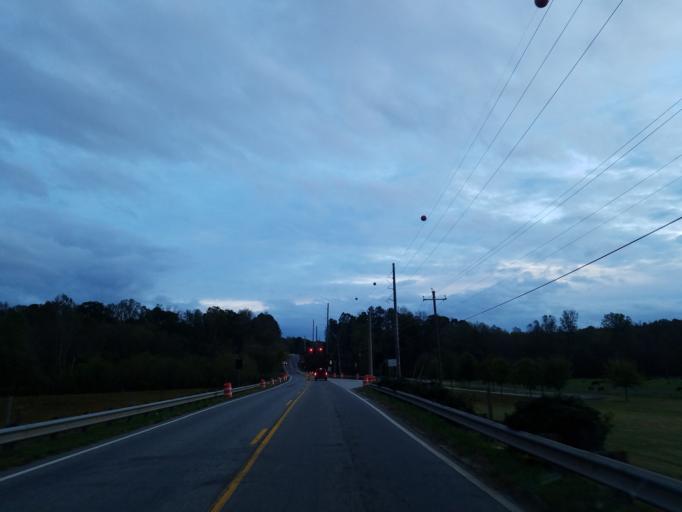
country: US
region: Georgia
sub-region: Dawson County
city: Dawsonville
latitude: 34.3599
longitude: -84.1135
